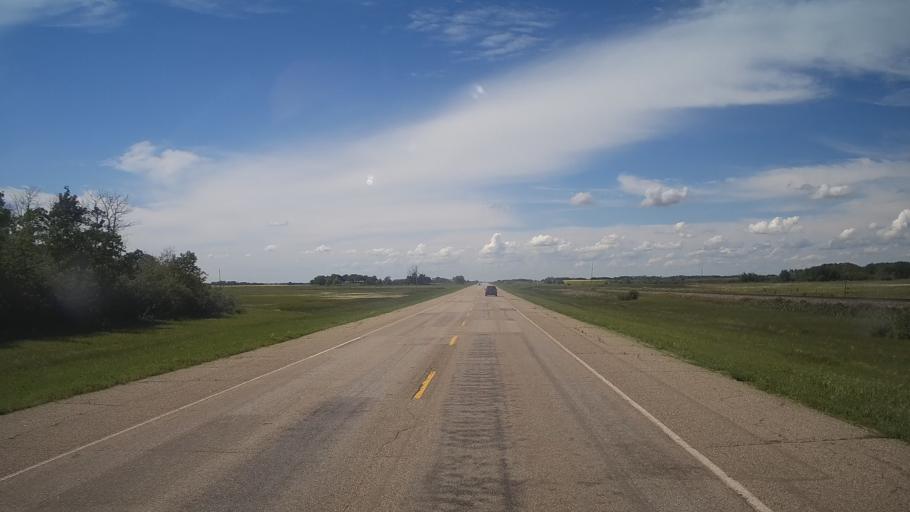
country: CA
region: Saskatchewan
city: Yorkton
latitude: 51.0640
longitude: -102.2116
